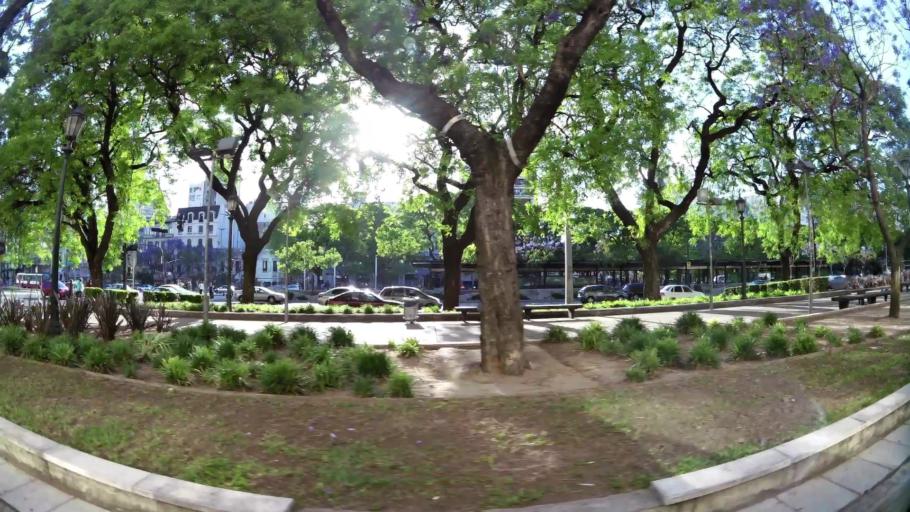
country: AR
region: Buenos Aires F.D.
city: Buenos Aires
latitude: -34.6079
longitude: -58.3808
